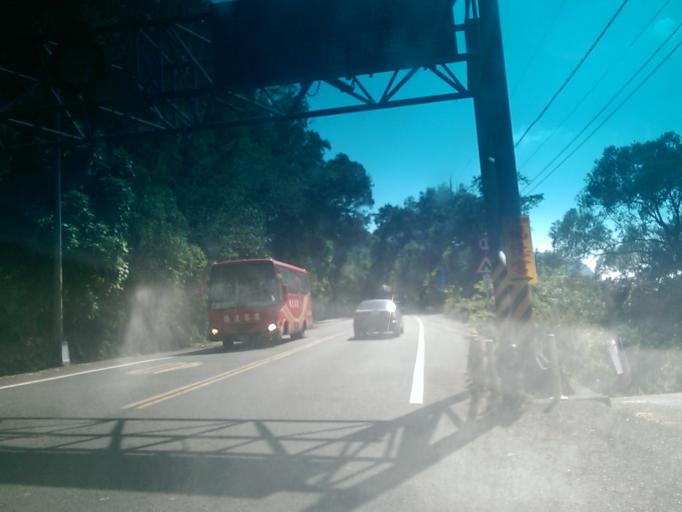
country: TW
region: Taiwan
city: Lugu
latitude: 23.8267
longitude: 120.7620
